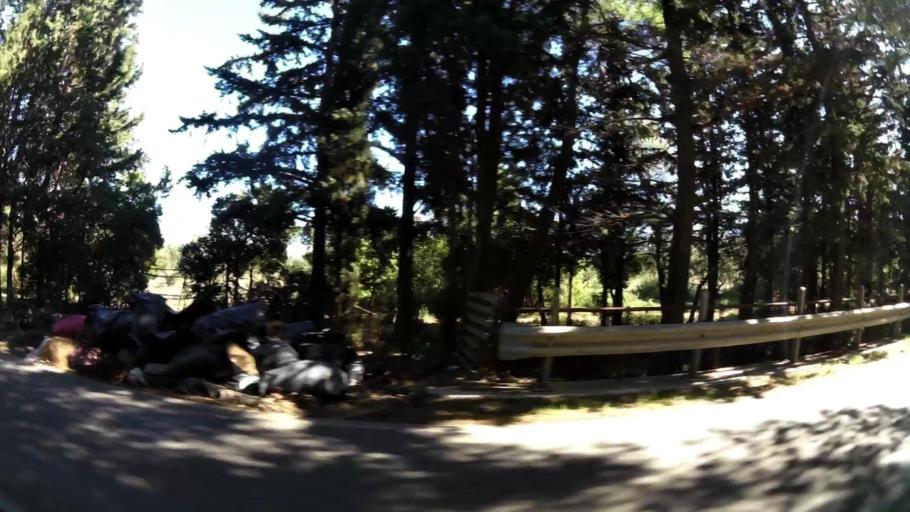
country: GR
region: Attica
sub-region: Nomarchia Athinas
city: Nea Erythraia
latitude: 38.1099
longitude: 23.8038
